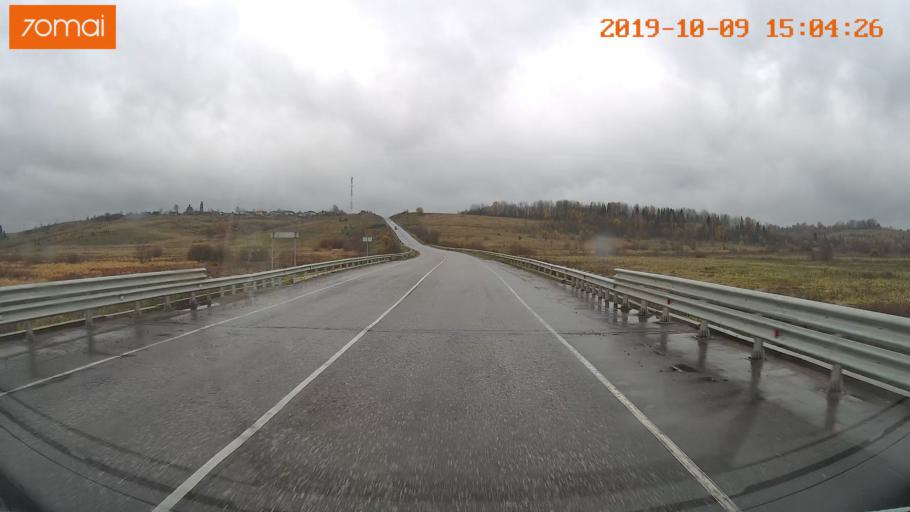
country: RU
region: Kostroma
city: Chistyye Bory
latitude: 58.2586
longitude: 41.6671
